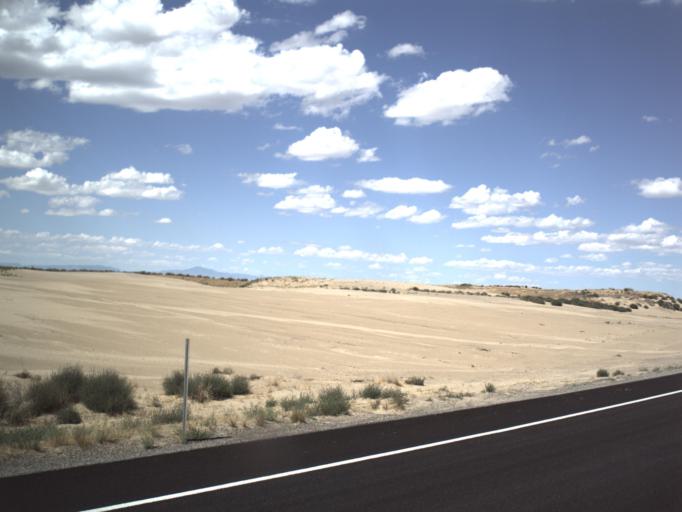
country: US
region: Utah
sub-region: Millard County
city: Fillmore
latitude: 39.1315
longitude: -112.3609
